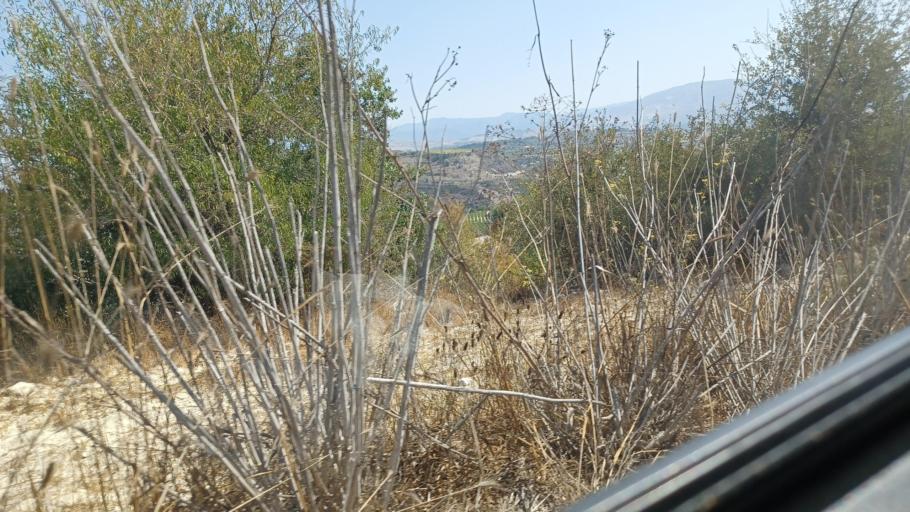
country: CY
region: Pafos
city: Tala
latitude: 34.8657
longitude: 32.4752
